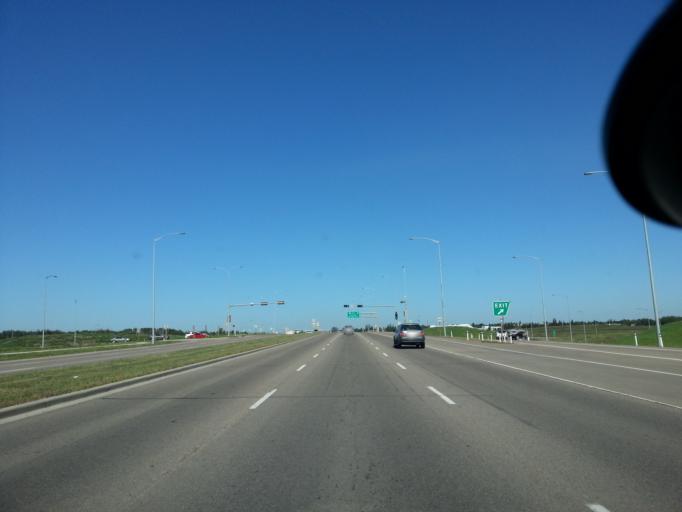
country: CA
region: Alberta
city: St. Albert
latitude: 53.6149
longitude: -113.5967
